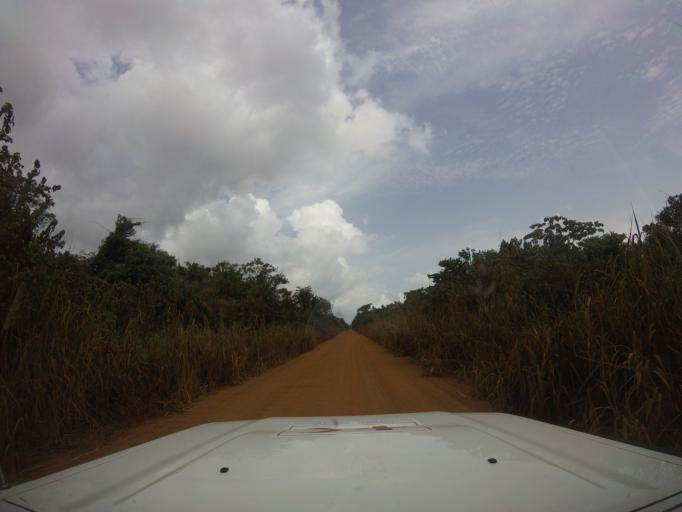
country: LR
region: Grand Cape Mount
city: Robertsport
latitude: 6.6832
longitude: -11.2405
